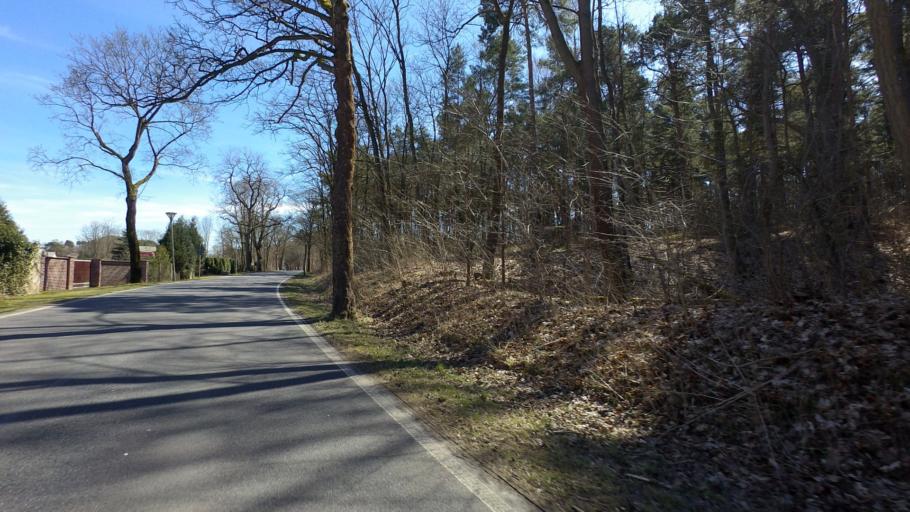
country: DE
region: Brandenburg
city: Halbe
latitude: 52.1113
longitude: 13.6807
